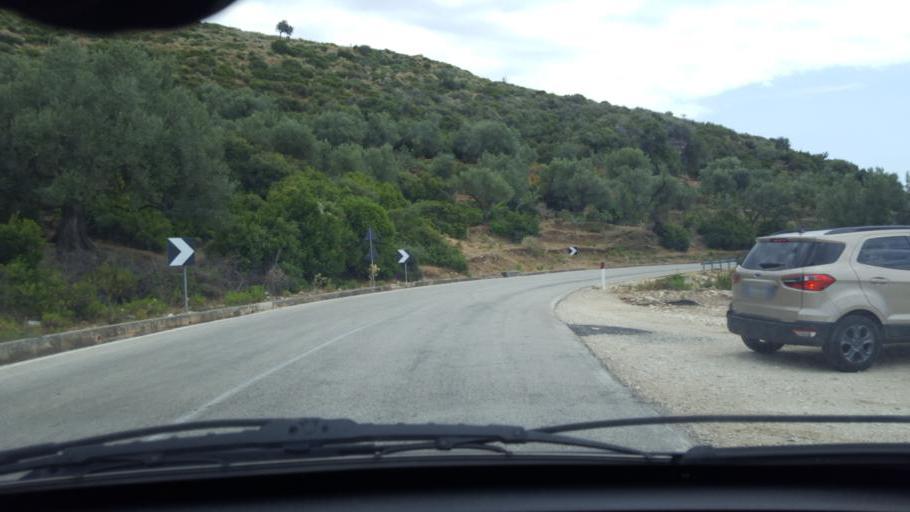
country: AL
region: Vlore
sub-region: Rrethi i Sarandes
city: Lukove
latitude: 40.0279
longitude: 19.8864
